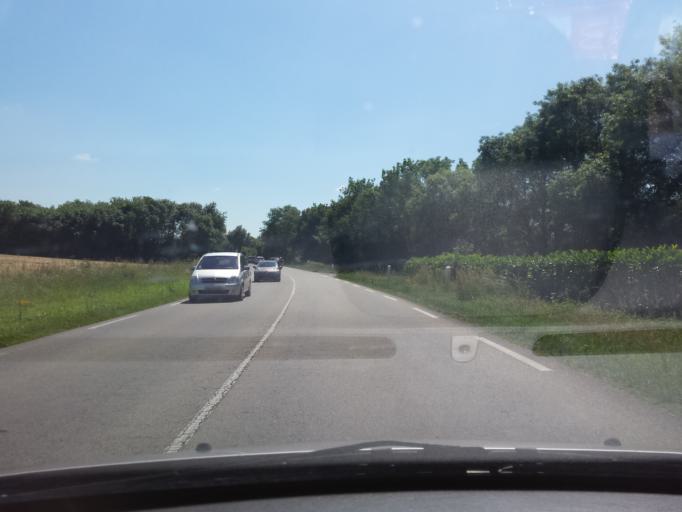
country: FR
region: Pays de la Loire
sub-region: Departement de la Loire-Atlantique
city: Machecoul
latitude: 46.9524
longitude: -1.8268
